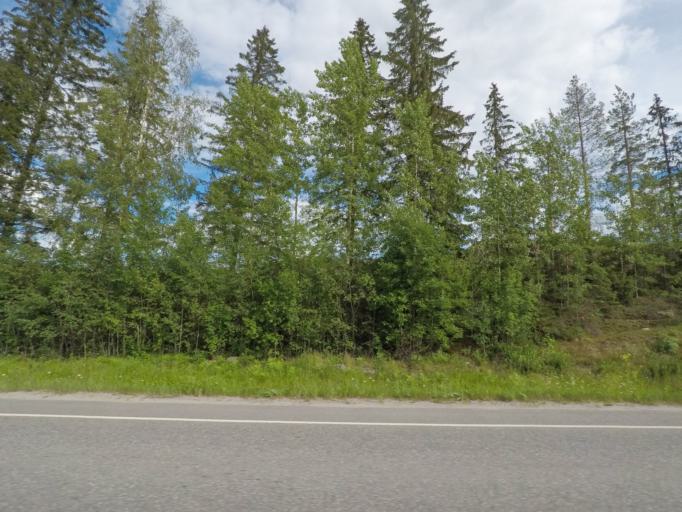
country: FI
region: Paijanne Tavastia
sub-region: Lahti
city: Lahti
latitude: 60.9327
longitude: 25.5872
